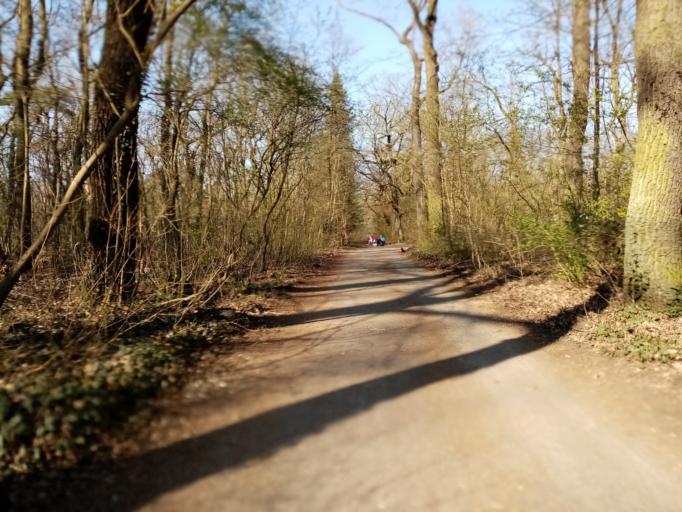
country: DE
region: Berlin
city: Karlshorst
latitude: 52.4660
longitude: 13.5423
